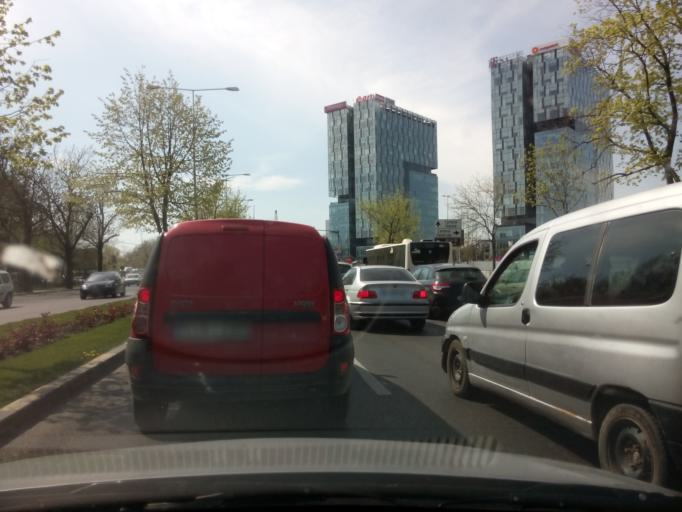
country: RO
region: Bucuresti
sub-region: Municipiul Bucuresti
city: Bucuresti
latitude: 44.4793
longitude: 26.0734
